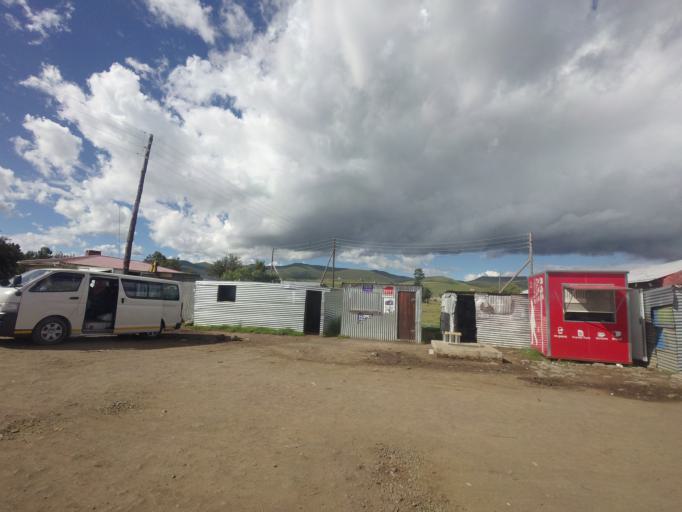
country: LS
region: Maseru
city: Nako
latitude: -29.8402
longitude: 28.0514
